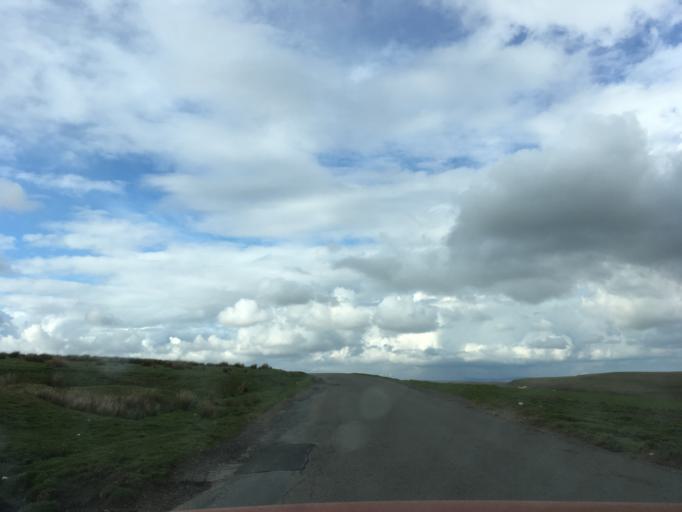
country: GB
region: Wales
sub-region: Caerphilly County Borough
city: Rhymney
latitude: 51.7258
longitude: -3.2974
